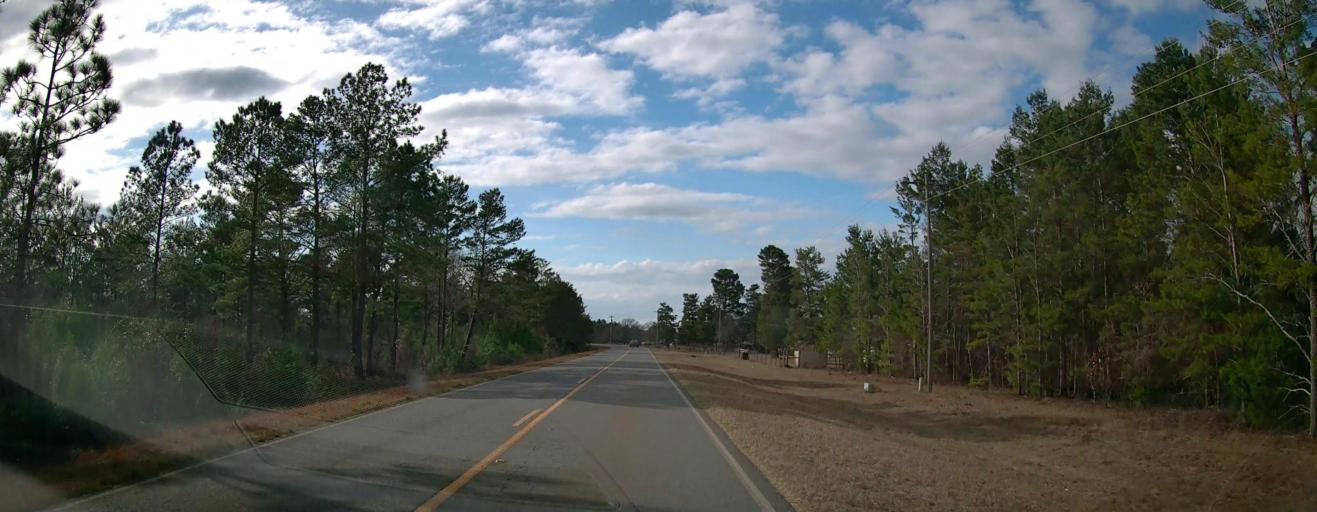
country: US
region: Georgia
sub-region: Talbot County
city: Talbotton
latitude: 32.4977
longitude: -84.5649
